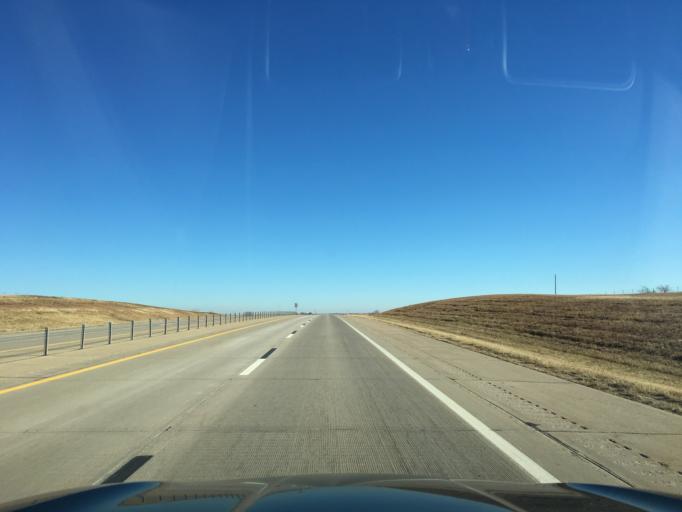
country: US
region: Oklahoma
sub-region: Noble County
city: Perry
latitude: 36.3920
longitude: -97.1527
